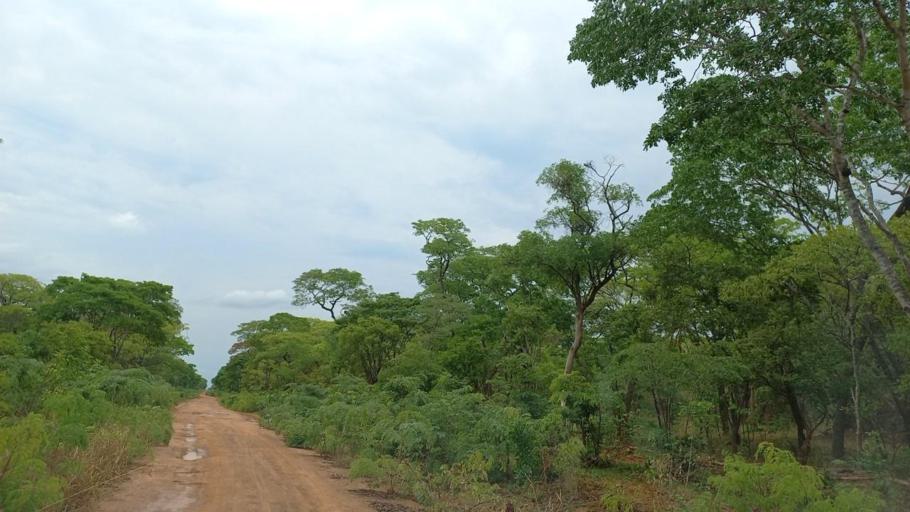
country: ZM
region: North-Western
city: Kalengwa
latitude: -13.6036
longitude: 24.9746
